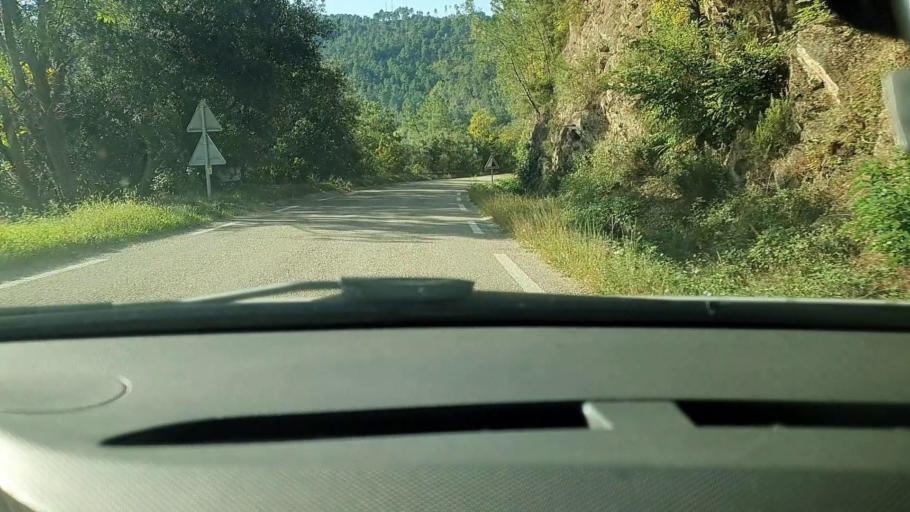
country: FR
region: Languedoc-Roussillon
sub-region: Departement du Gard
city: Besseges
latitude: 44.2968
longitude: 4.0673
